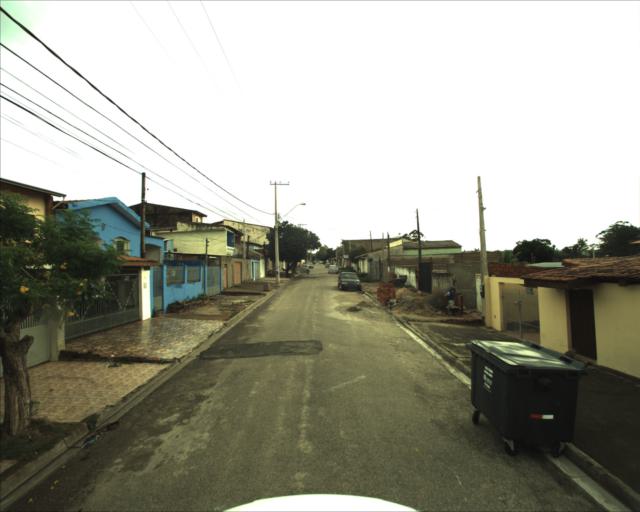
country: BR
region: Sao Paulo
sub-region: Sorocaba
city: Sorocaba
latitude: -23.5064
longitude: -47.4993
